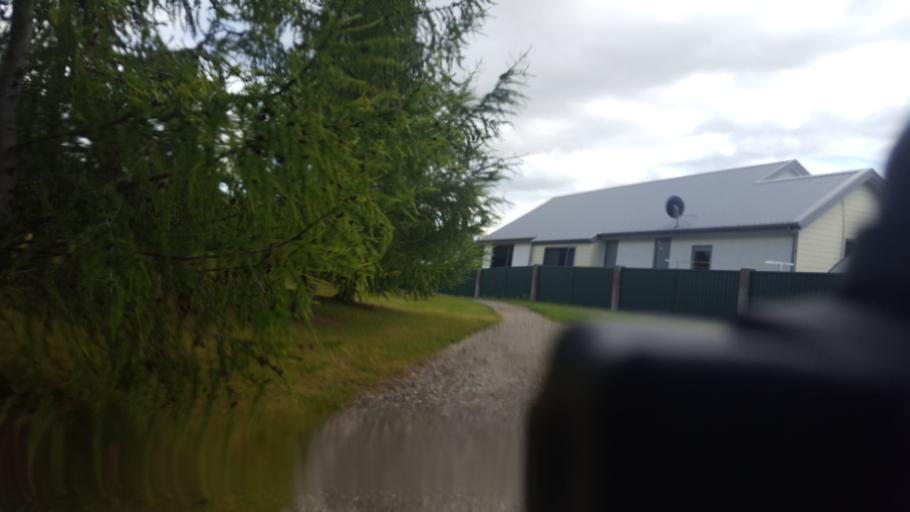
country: NZ
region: Otago
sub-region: Queenstown-Lakes District
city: Wanaka
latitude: -45.2421
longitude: 169.3777
